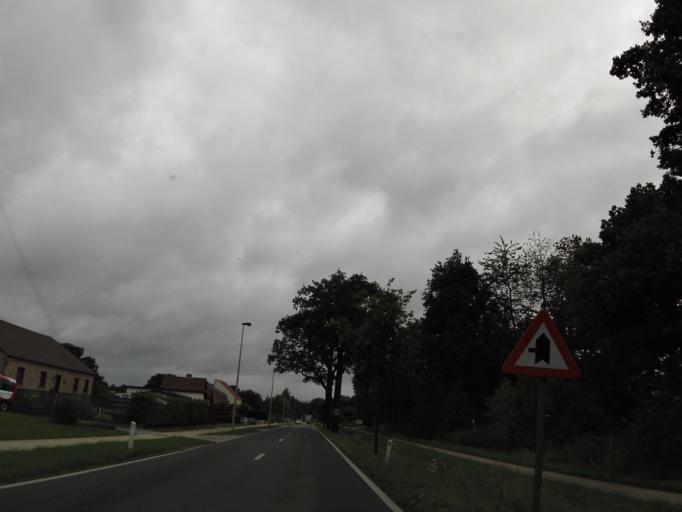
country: BE
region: Flanders
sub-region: Provincie Limburg
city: Bree
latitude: 51.1058
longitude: 5.5911
